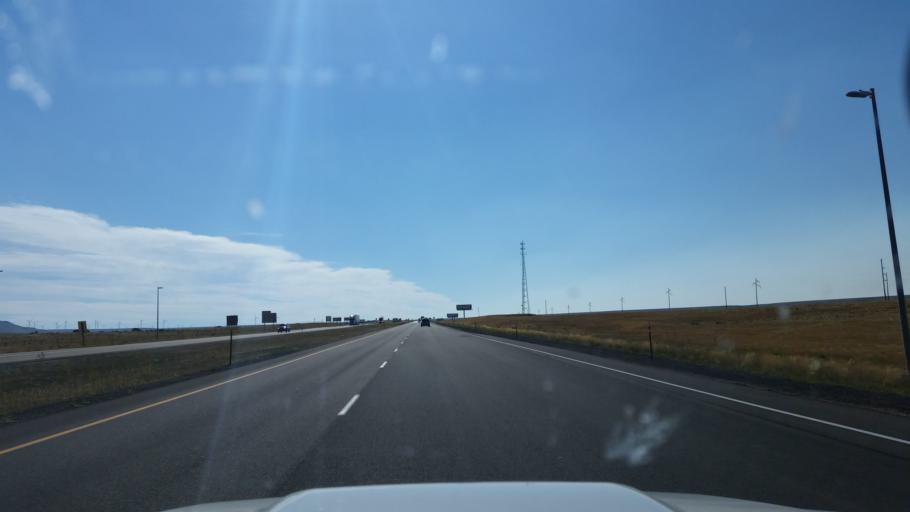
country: US
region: Wyoming
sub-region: Uinta County
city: Mountain View
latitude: 41.3308
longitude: -110.4356
